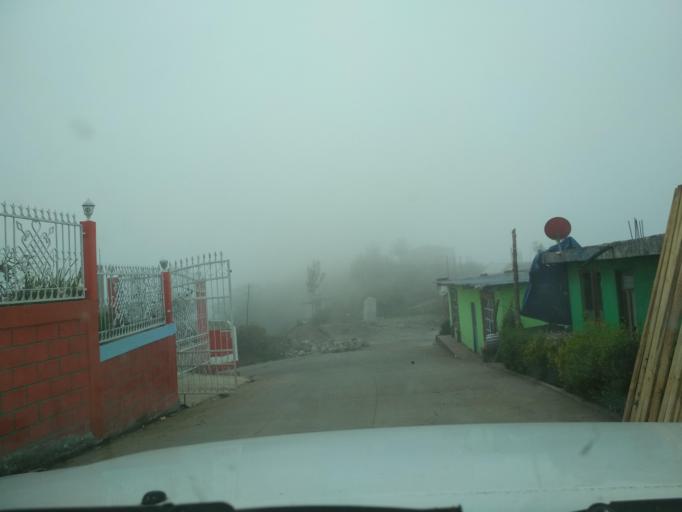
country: MX
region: Veracruz
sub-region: La Perla
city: Chilapa
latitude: 18.9809
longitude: -97.1858
